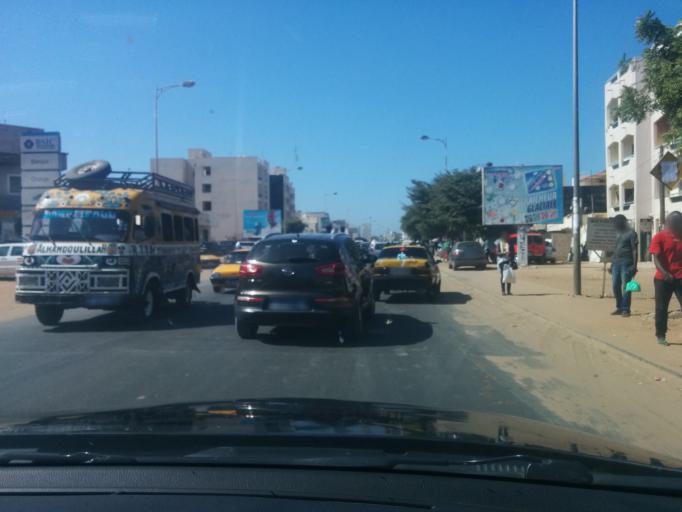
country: SN
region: Dakar
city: Grand Dakar
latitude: 14.7515
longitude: -17.4377
